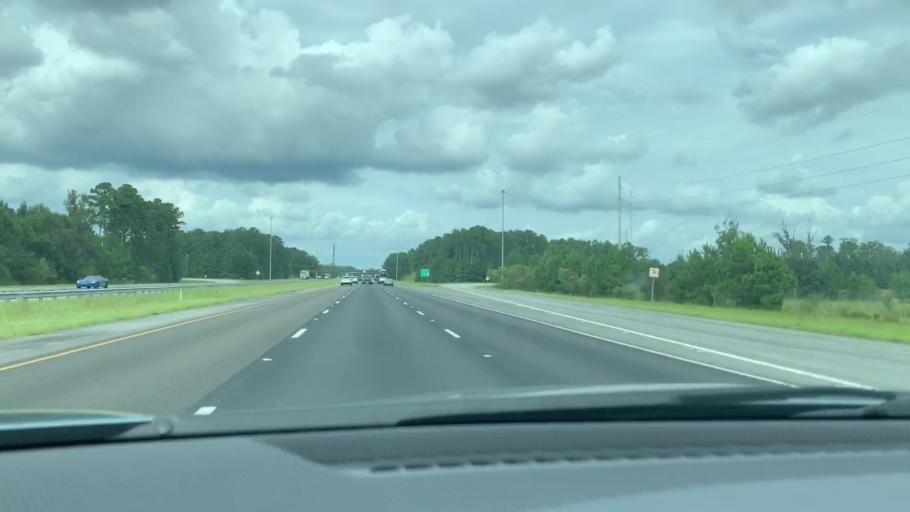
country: US
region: Georgia
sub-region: Liberty County
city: Midway
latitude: 31.7728
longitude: -81.3796
